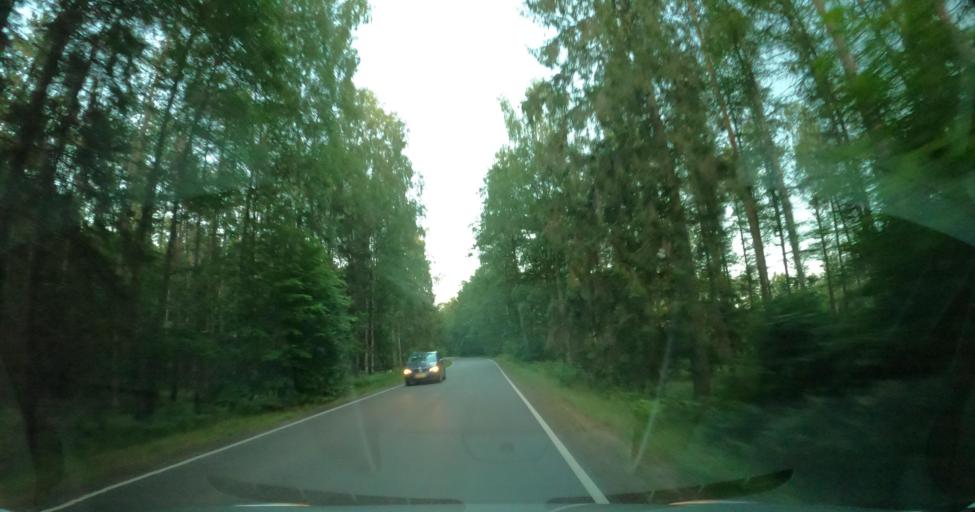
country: PL
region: Pomeranian Voivodeship
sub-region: Powiat leborski
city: Lebork
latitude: 54.5024
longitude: 17.8211
